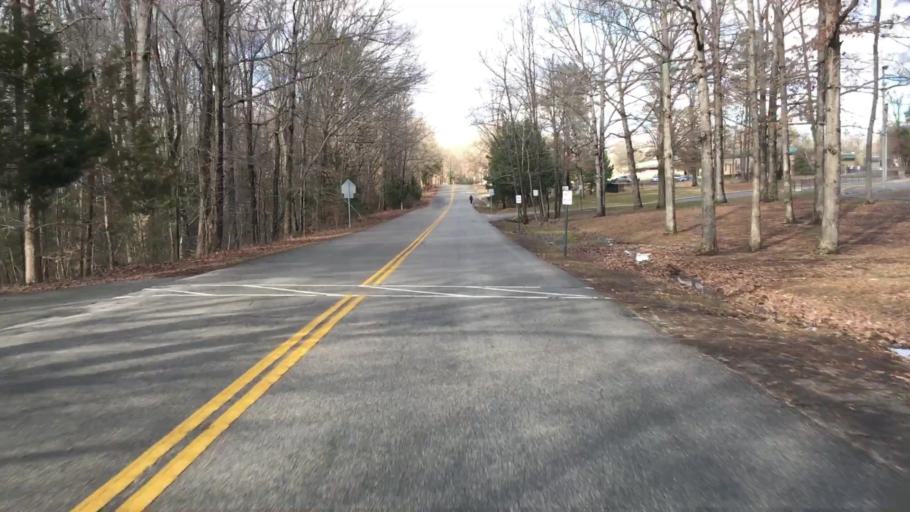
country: US
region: Virginia
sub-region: Chesterfield County
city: Bon Air
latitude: 37.5290
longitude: -77.6149
